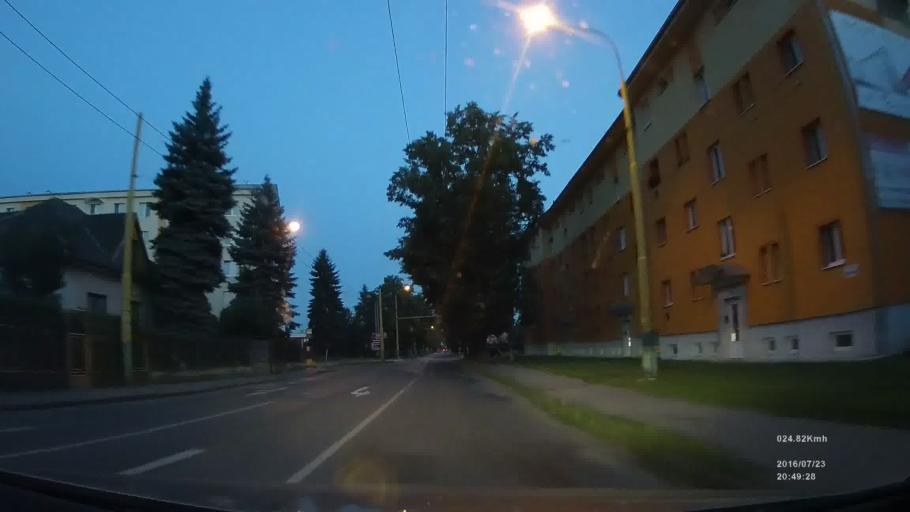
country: SK
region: Presovsky
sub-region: Okres Presov
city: Presov
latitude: 48.9866
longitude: 21.2427
